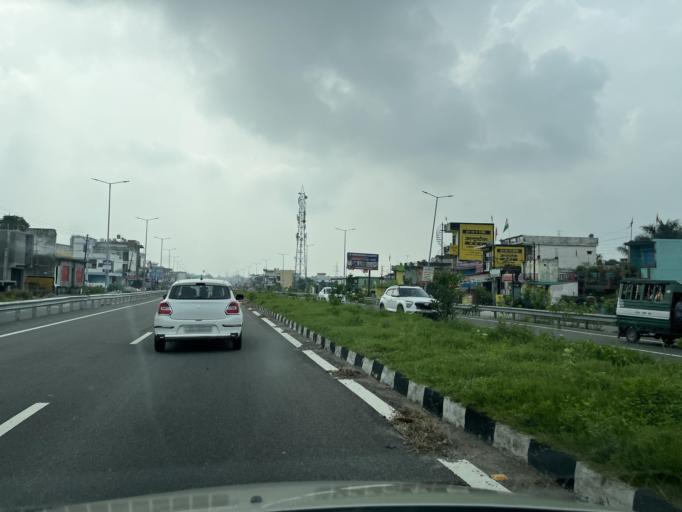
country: IN
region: Uttarakhand
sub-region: Dehradun
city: Raiwala
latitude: 30.0774
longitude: 78.1955
